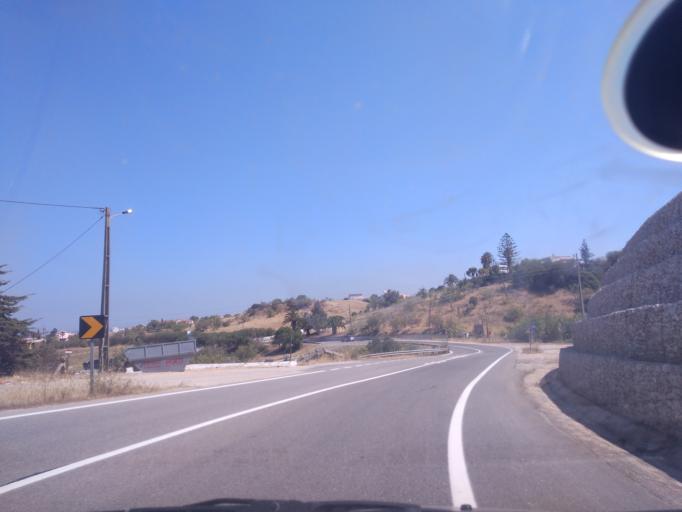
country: PT
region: Faro
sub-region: Lagos
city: Lagos
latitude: 37.1156
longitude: -8.6865
